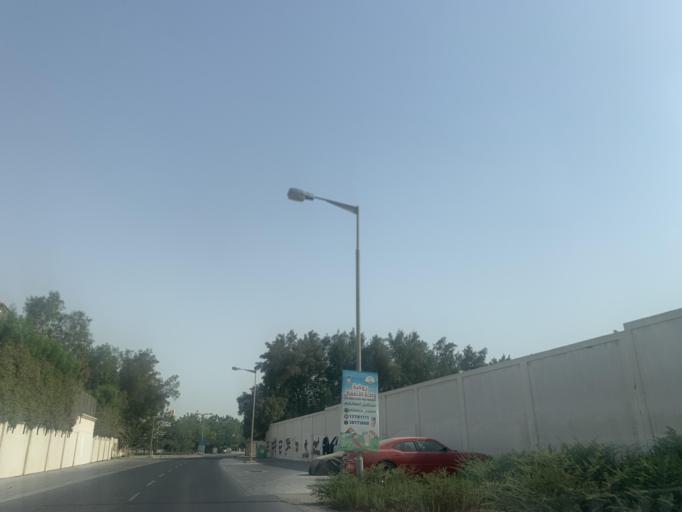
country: BH
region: Manama
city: Jidd Hafs
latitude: 26.2141
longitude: 50.4738
